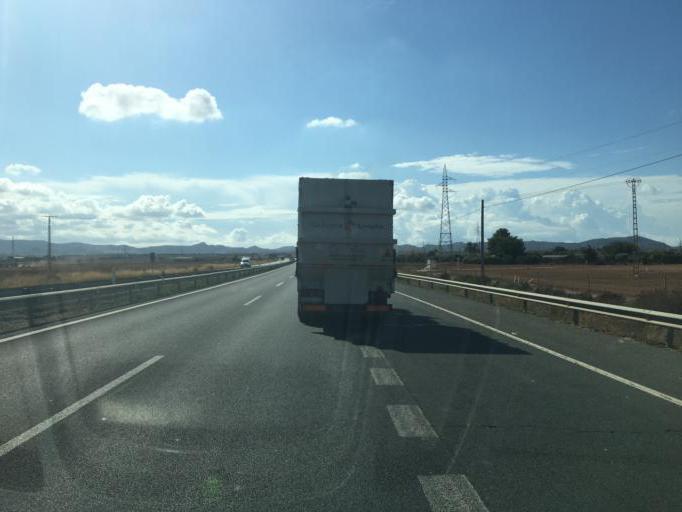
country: ES
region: Murcia
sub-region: Murcia
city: Cartagena
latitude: 37.6539
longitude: -0.9784
